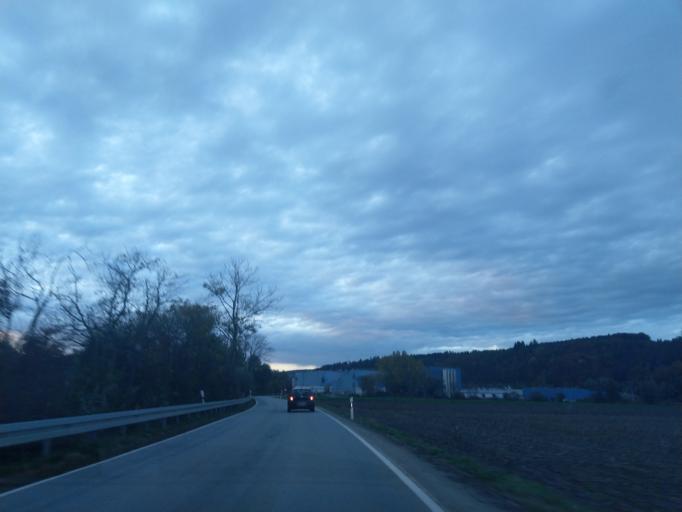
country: DE
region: Bavaria
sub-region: Lower Bavaria
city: Niederalteich
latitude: 48.7877
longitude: 13.0186
